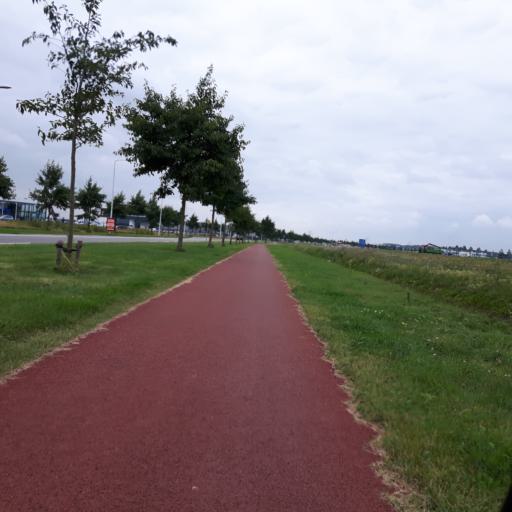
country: NL
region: Zeeland
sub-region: Gemeente Goes
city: Goes
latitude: 51.4826
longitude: 3.8929
